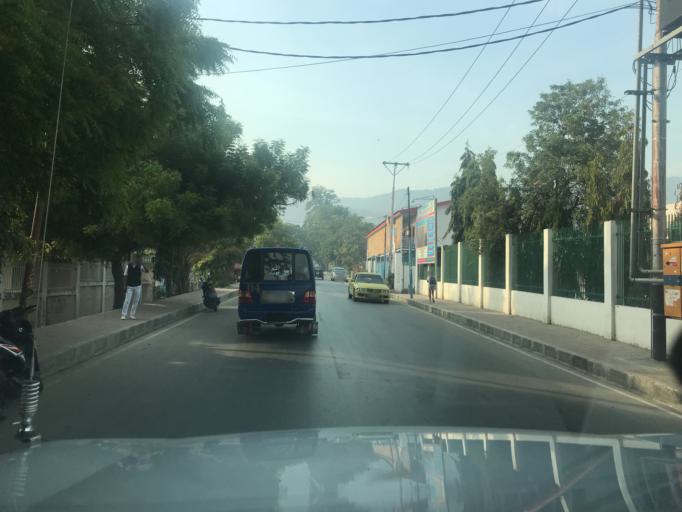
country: TL
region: Dili
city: Dili
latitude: -8.5624
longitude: 125.5807
